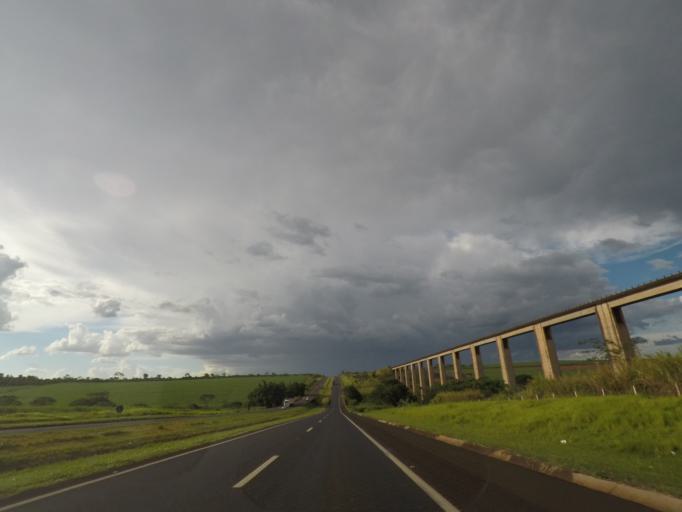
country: BR
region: Sao Paulo
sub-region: Jardinopolis
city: Jardinopolis
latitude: -21.0105
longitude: -47.8452
